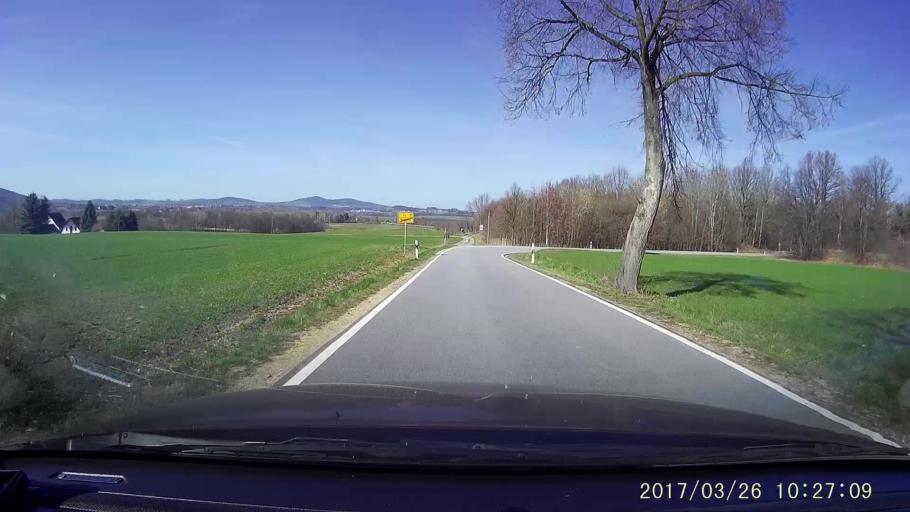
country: DE
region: Saxony
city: Sohland am Rotstein
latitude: 51.1174
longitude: 14.7384
